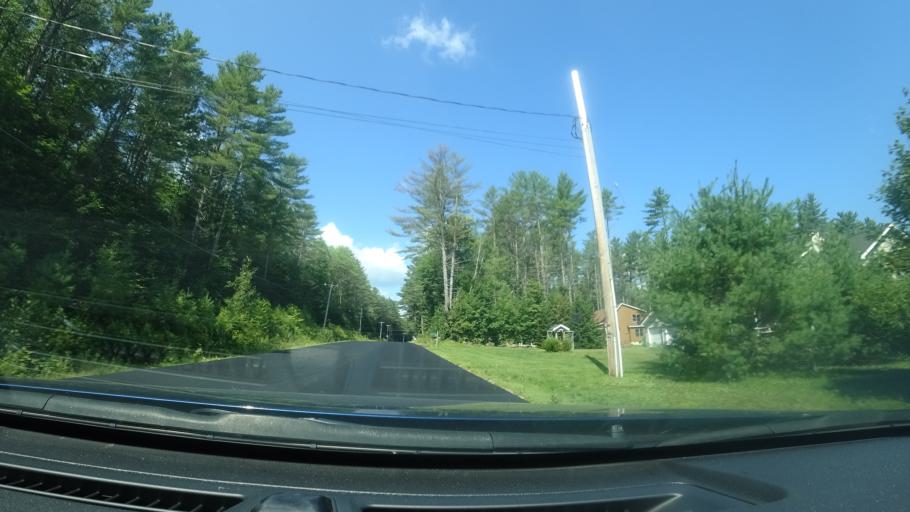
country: US
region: New York
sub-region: Warren County
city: Warrensburg
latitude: 43.6518
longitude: -73.8155
